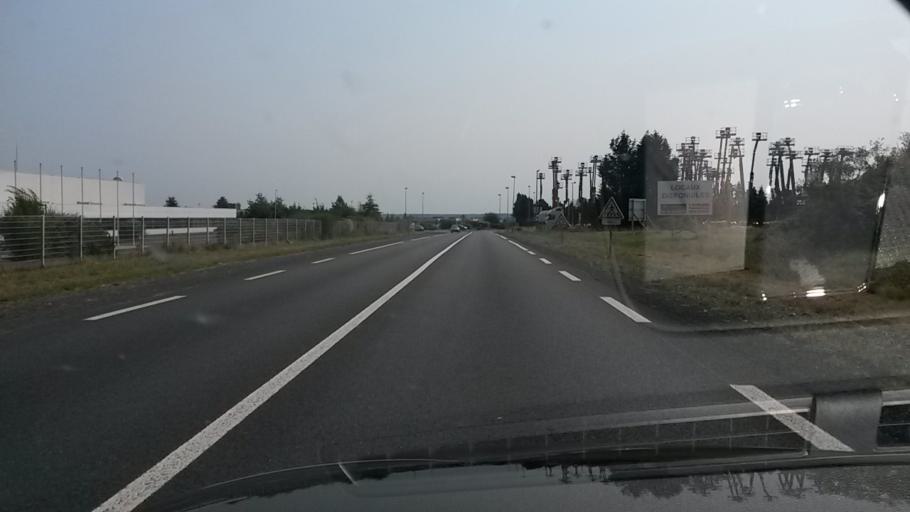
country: FR
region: Pays de la Loire
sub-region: Departement de la Loire-Atlantique
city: Mesanger
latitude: 47.4121
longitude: -1.1900
